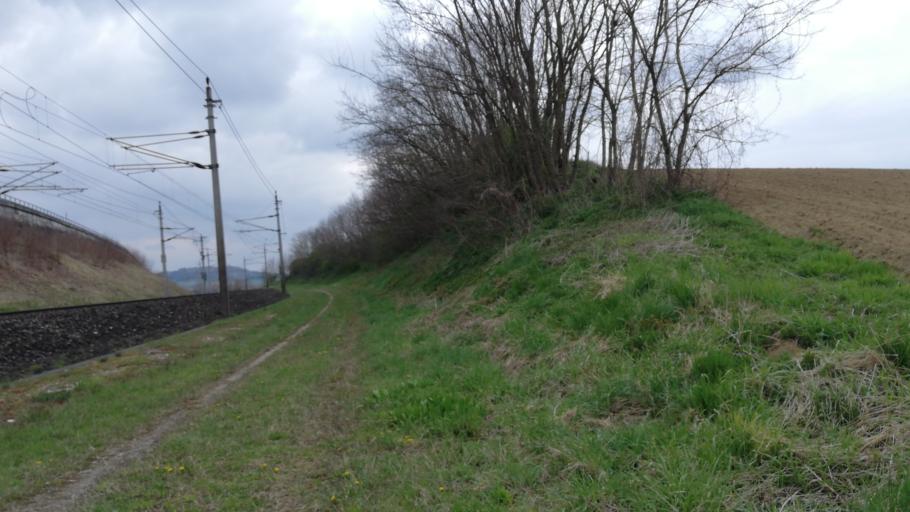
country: AT
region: Upper Austria
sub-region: Politischer Bezirk Grieskirchen
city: Bad Schallerbach
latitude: 48.2164
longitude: 13.9673
